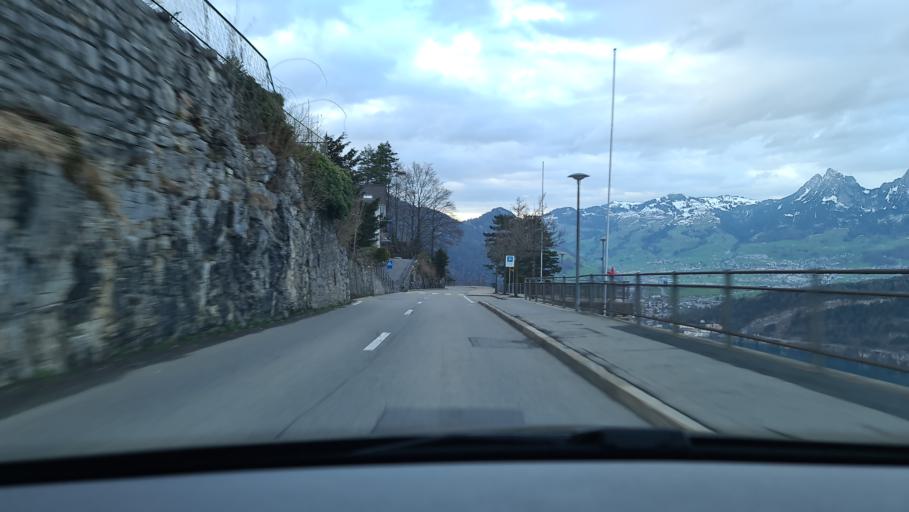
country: CH
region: Uri
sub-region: Uri
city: Bauen
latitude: 46.9711
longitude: 8.5870
